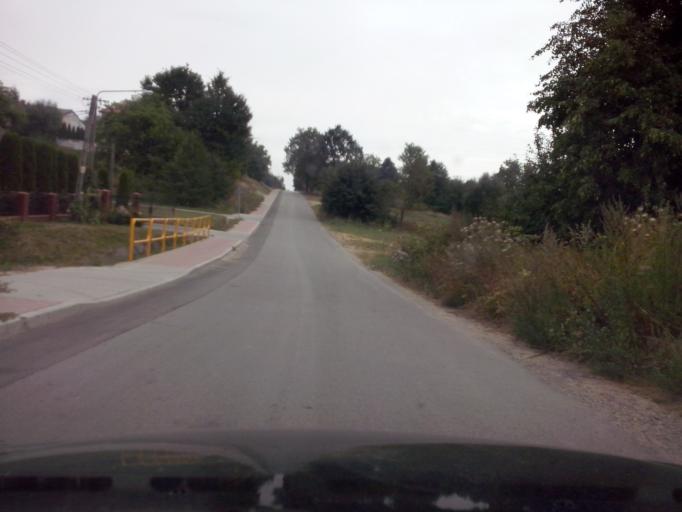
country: PL
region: Swietokrzyskie
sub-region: Powiat kielecki
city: Lagow
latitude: 50.7342
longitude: 21.0789
